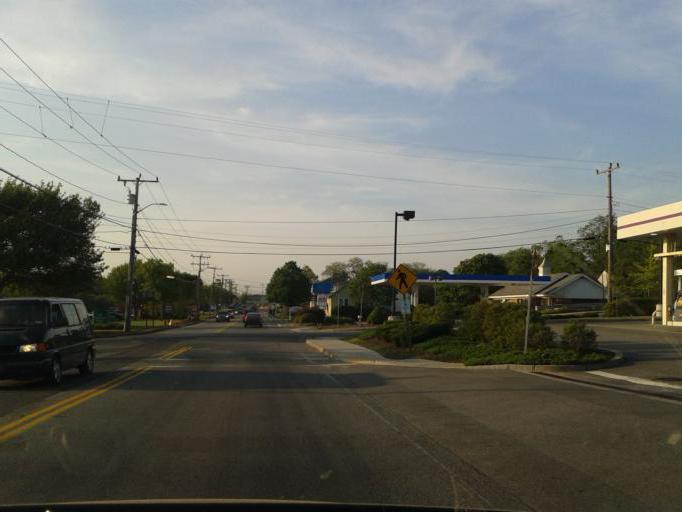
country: US
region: Massachusetts
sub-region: Barnstable County
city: Teaticket
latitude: 41.5569
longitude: -70.5997
